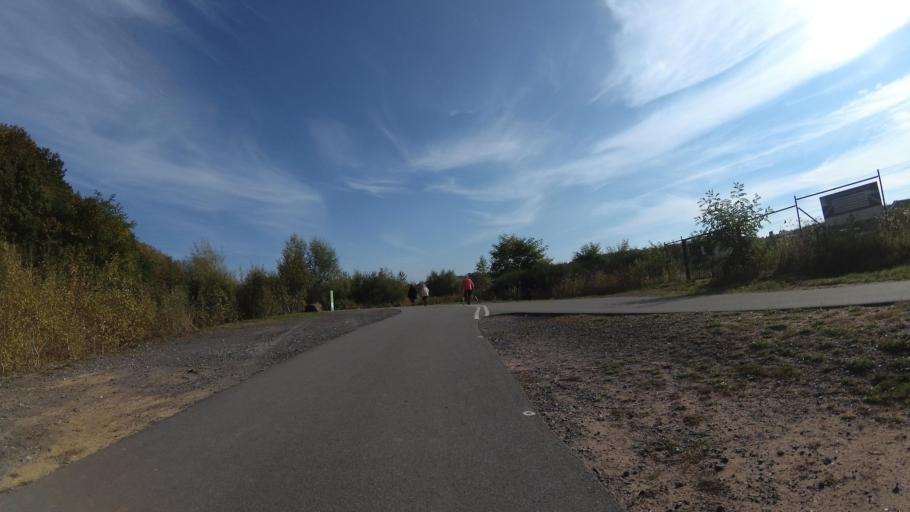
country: DE
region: Saarland
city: Friedrichsthal
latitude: 49.3443
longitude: 7.1147
